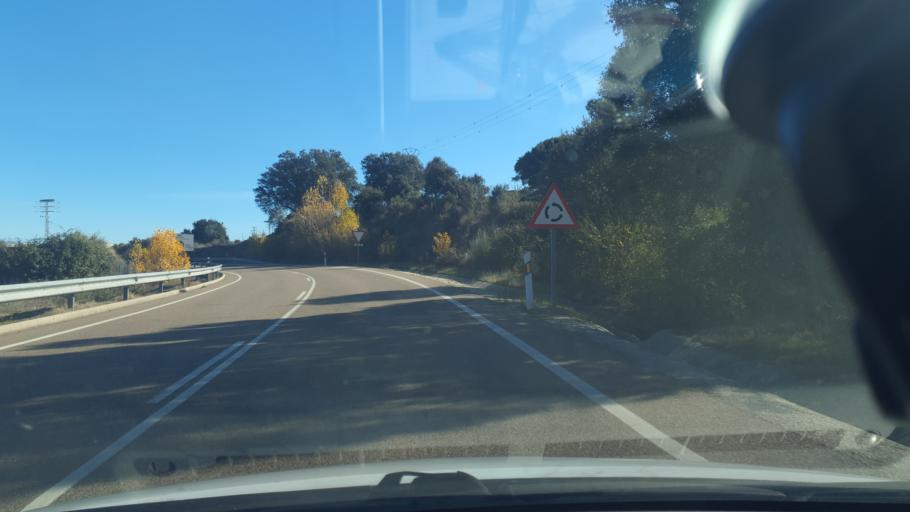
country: ES
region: Castille and Leon
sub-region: Provincia de Avila
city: Arenas de San Pedro
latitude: 40.1788
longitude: -5.0430
